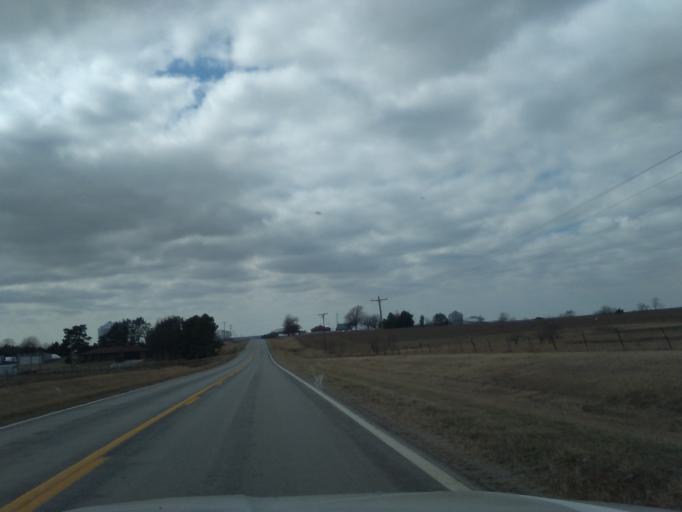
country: US
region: Nebraska
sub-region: Gage County
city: Wymore
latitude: 40.0448
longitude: -96.5067
